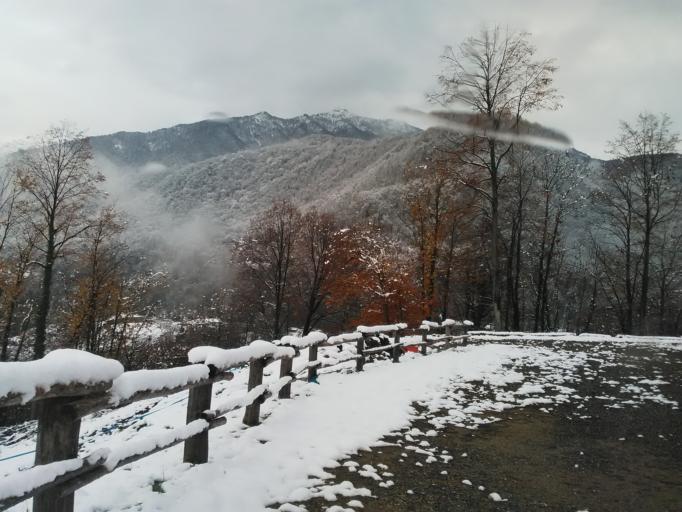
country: IT
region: Piedmont
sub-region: Provincia di Vercelli
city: Varallo
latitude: 45.7869
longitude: 8.2579
